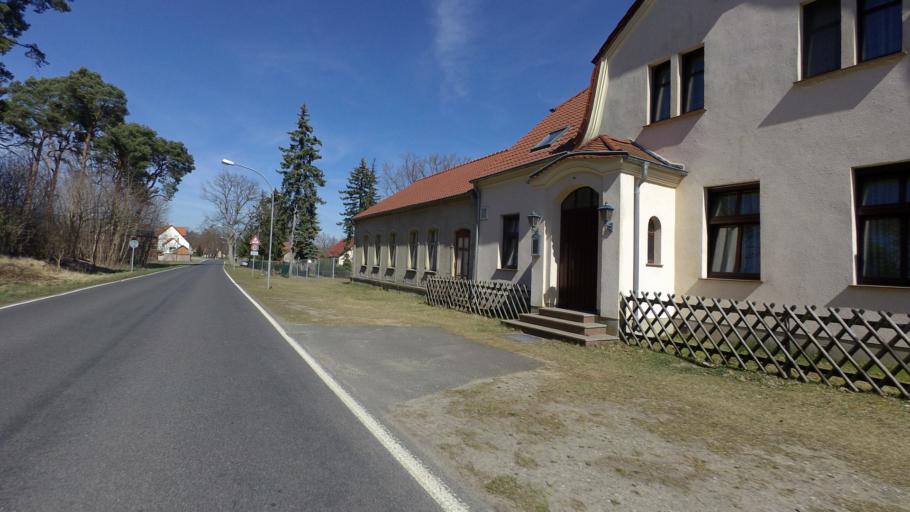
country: DE
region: Brandenburg
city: Storkow
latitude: 52.1920
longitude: 13.9185
